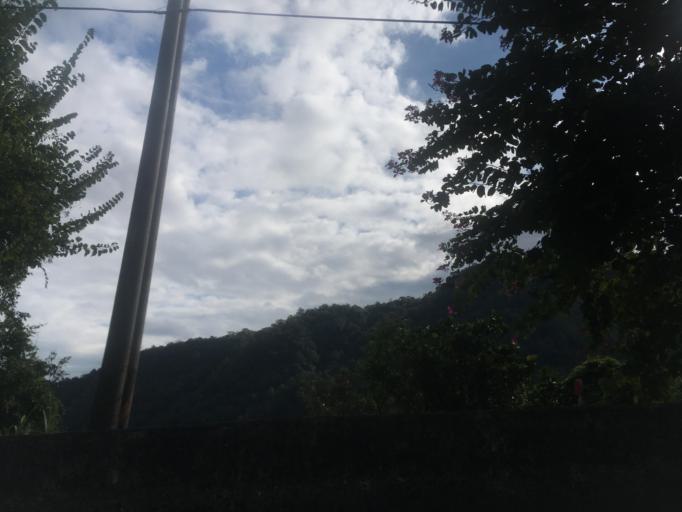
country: TW
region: Taiwan
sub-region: Yilan
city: Yilan
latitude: 24.6370
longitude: 121.5530
